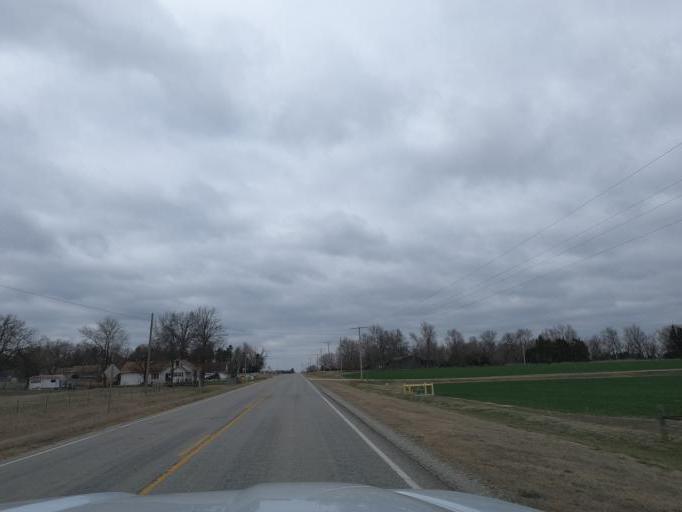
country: US
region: Kansas
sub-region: McPherson County
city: Inman
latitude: 38.2127
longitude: -97.7759
